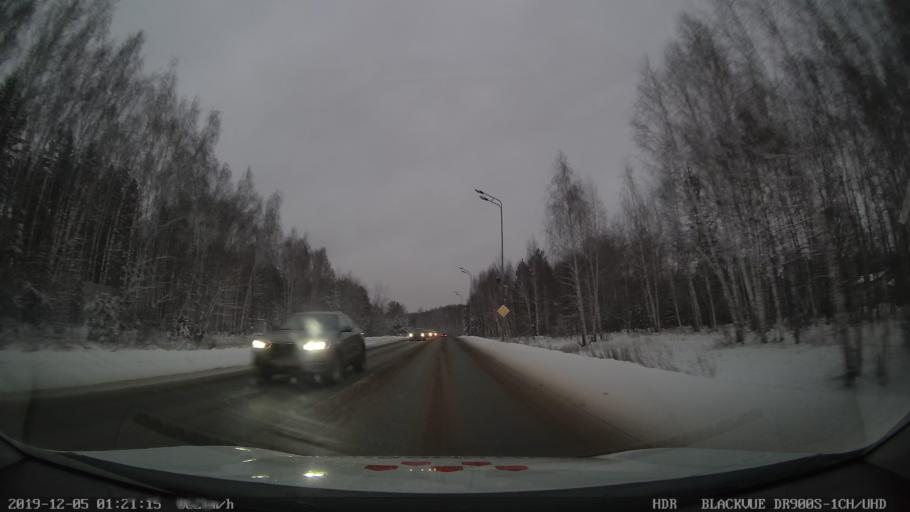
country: RU
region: Tatarstan
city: Stolbishchi
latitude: 55.6803
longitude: 49.1277
